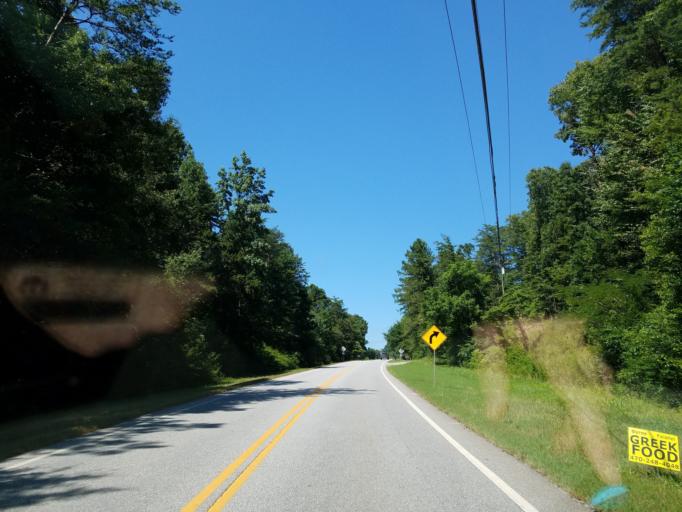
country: US
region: Georgia
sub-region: Dawson County
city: Dawsonville
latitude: 34.3961
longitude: -83.9890
